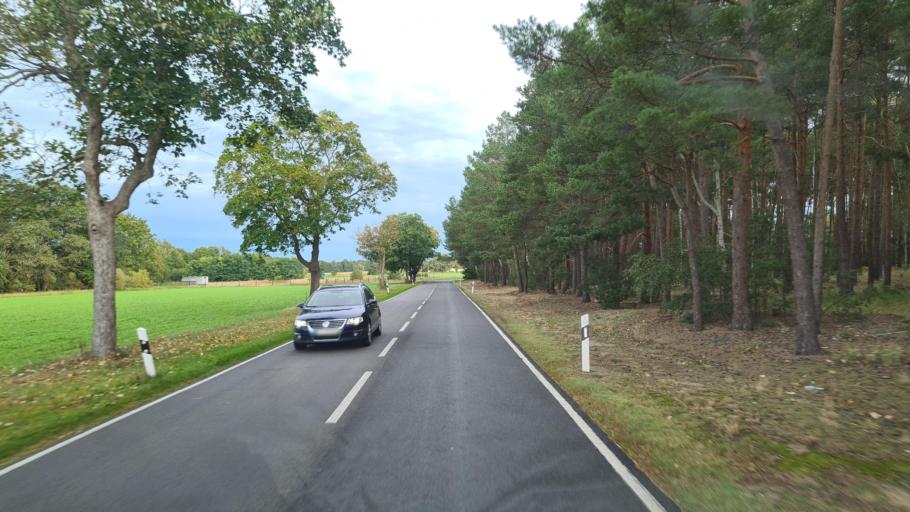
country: DE
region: Brandenburg
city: Kasel-Golzig
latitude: 51.9226
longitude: 13.7100
